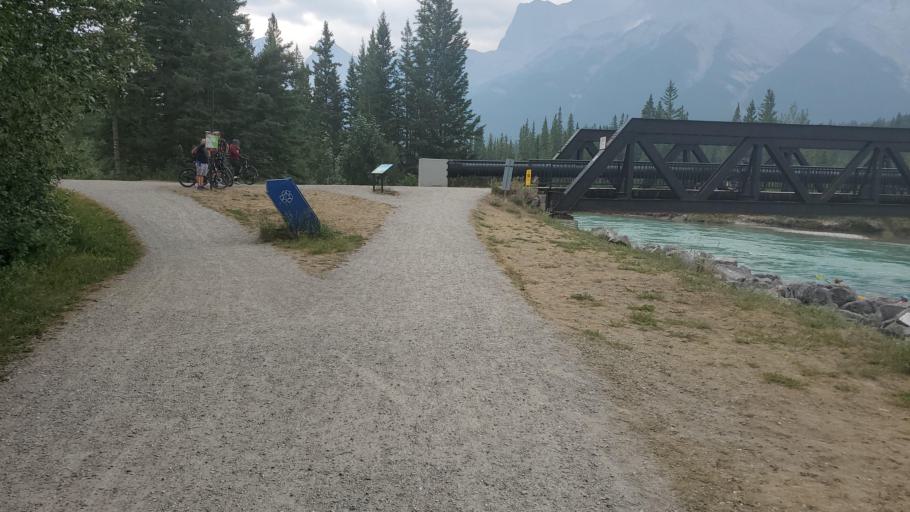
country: CA
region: Alberta
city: Canmore
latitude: 51.0919
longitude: -115.3694
